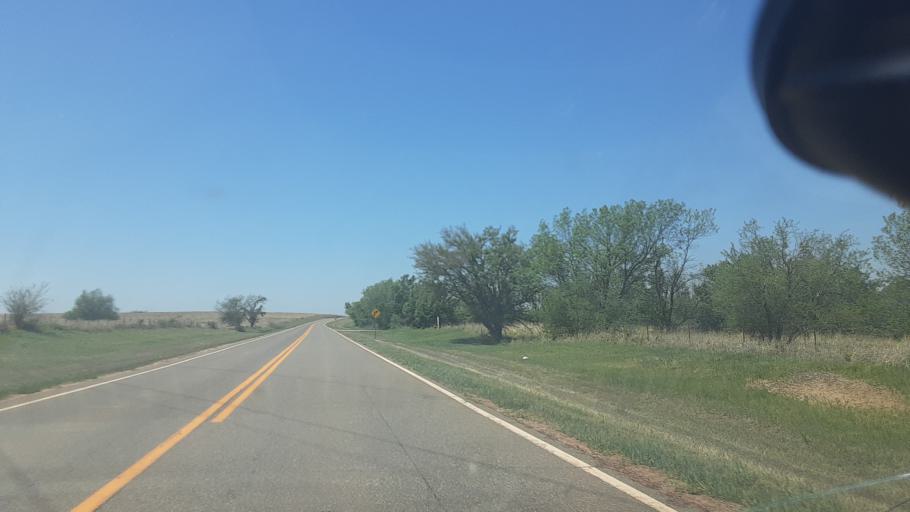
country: US
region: Oklahoma
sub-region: Noble County
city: Perry
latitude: 36.1129
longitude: -97.3794
